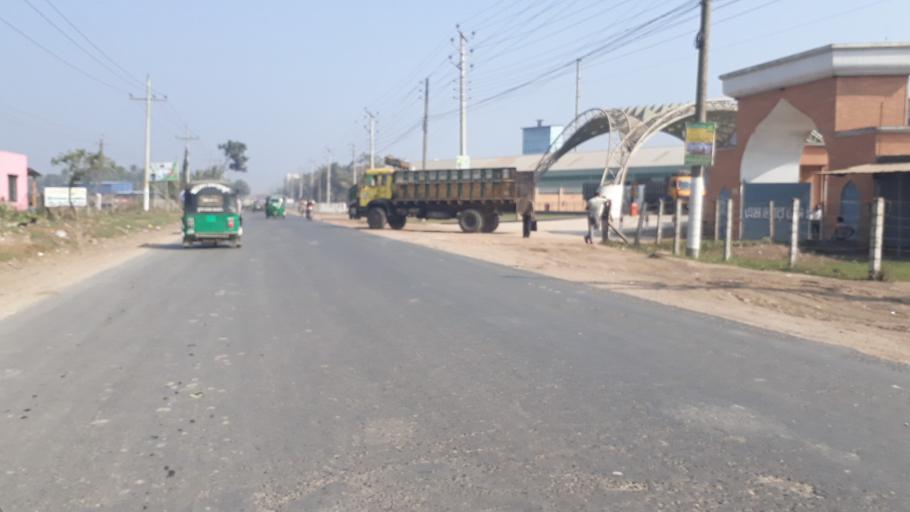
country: BD
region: Khulna
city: Kushtia
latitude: 23.8824
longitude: 89.0971
